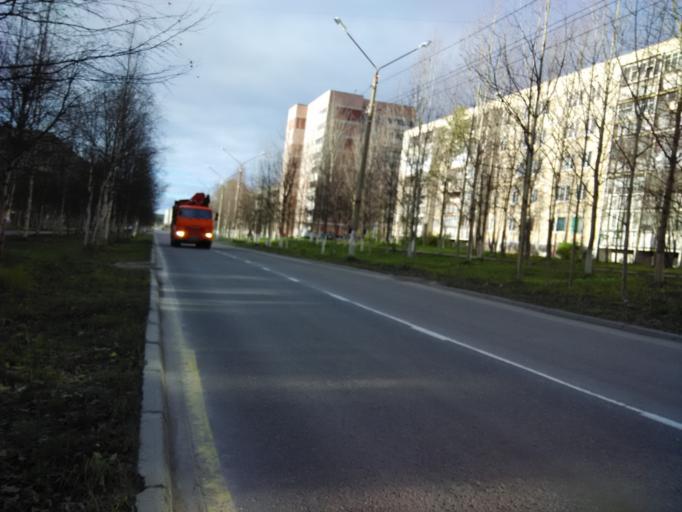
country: RU
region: Murmansk
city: Polyarnyye Zori
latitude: 67.3696
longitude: 32.4944
